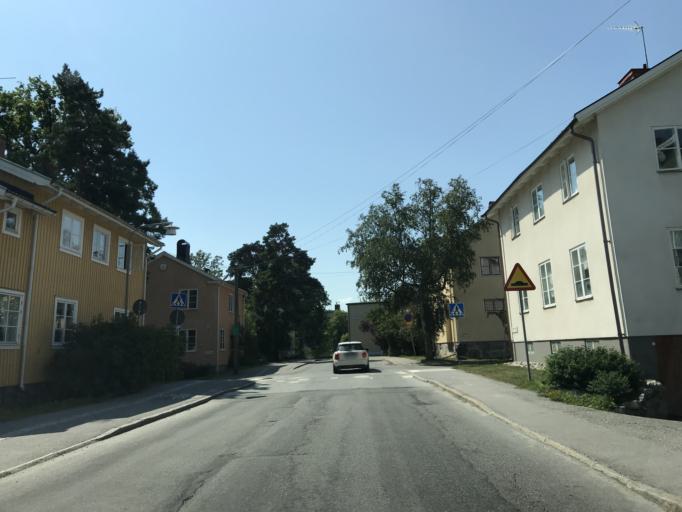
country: SE
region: Stockholm
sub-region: Stockholms Kommun
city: Bromma
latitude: 59.3334
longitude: 17.9621
